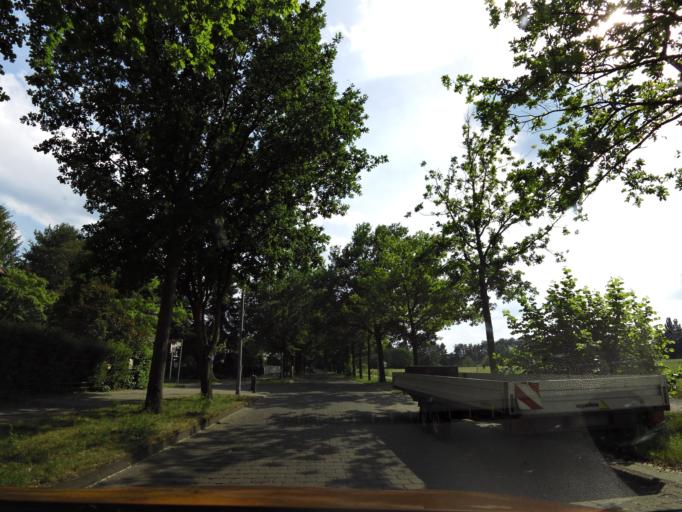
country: DE
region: Berlin
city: Heiligensee
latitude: 52.6096
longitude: 13.2308
